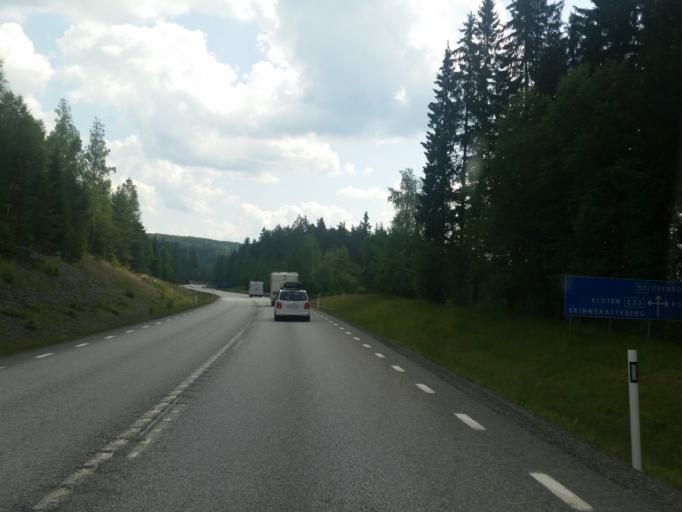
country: SE
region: OErebro
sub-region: Ljusnarsbergs Kommun
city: Kopparberg
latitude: 59.8723
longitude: 15.0418
